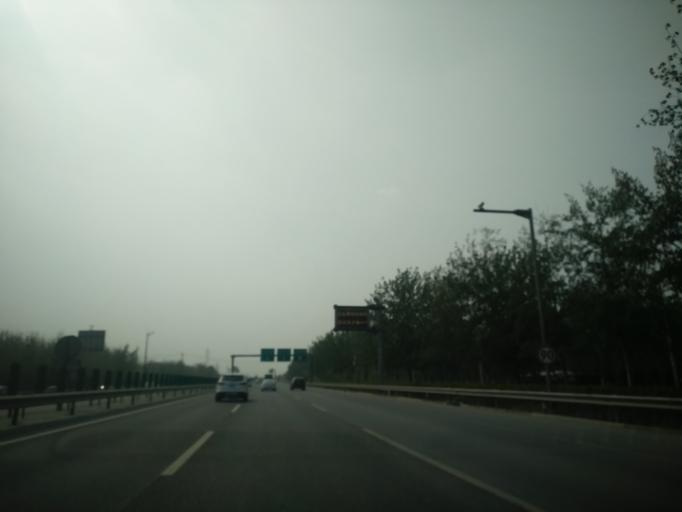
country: CN
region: Beijing
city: Taihu
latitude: 39.8670
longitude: 116.5660
